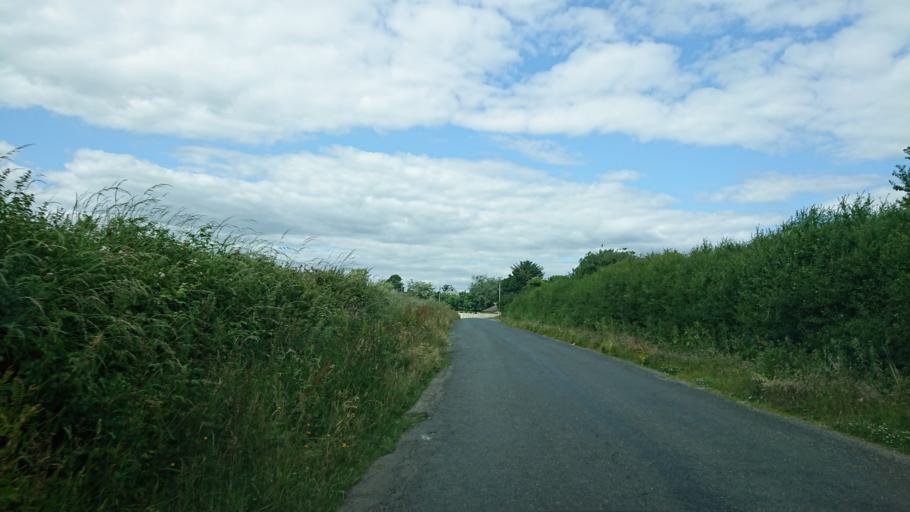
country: IE
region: Munster
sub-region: Waterford
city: Tra Mhor
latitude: 52.2187
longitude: -7.1578
